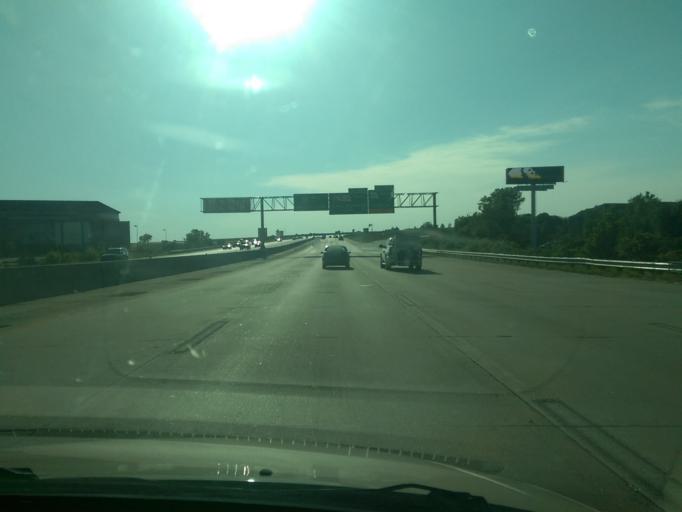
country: US
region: Missouri
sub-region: Jackson County
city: East Independence
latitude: 39.0407
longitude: -94.3537
